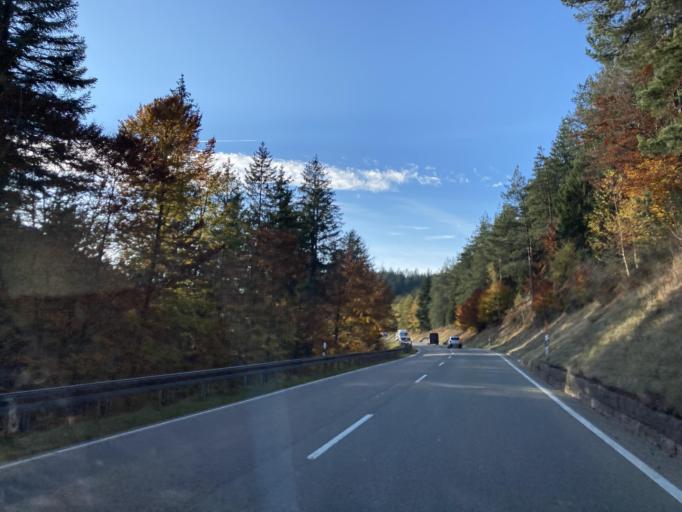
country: DE
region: Baden-Wuerttemberg
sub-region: Karlsruhe Region
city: Baiersbronn
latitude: 48.4617
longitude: 8.3670
